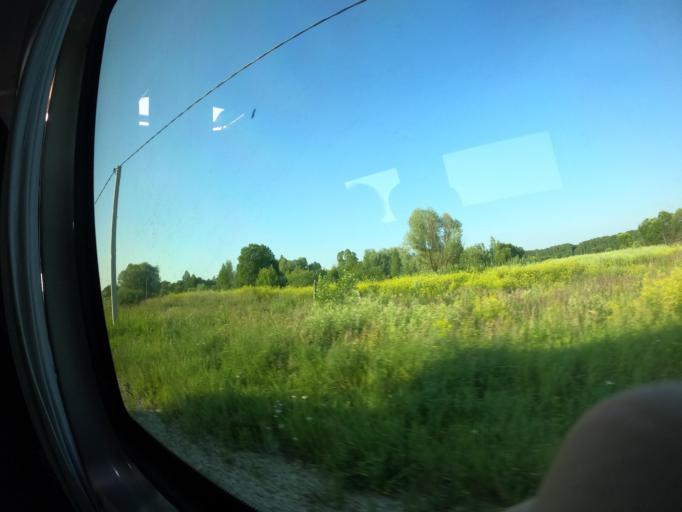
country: RU
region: Moskovskaya
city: Obolensk
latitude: 54.9332
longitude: 37.2499
